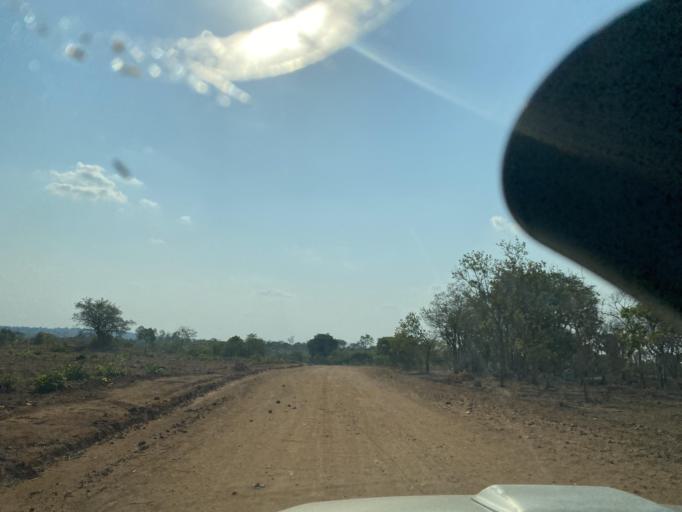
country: ZM
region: Lusaka
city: Chongwe
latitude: -15.3159
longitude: 28.7129
